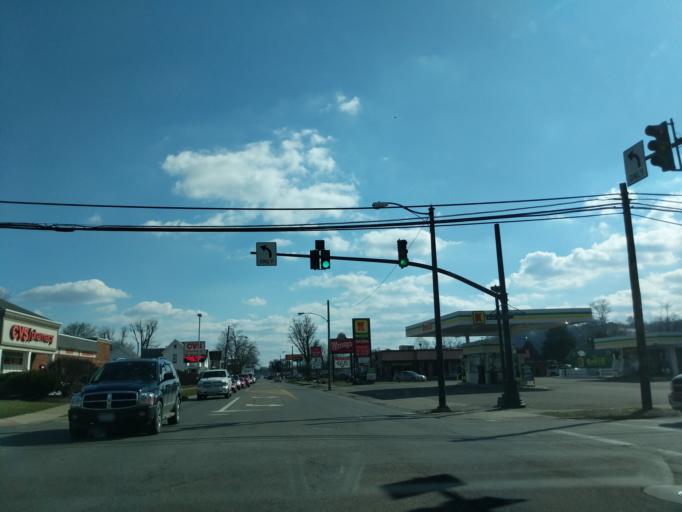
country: US
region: Ohio
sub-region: Coshocton County
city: Coshocton
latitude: 40.2725
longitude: -81.8689
